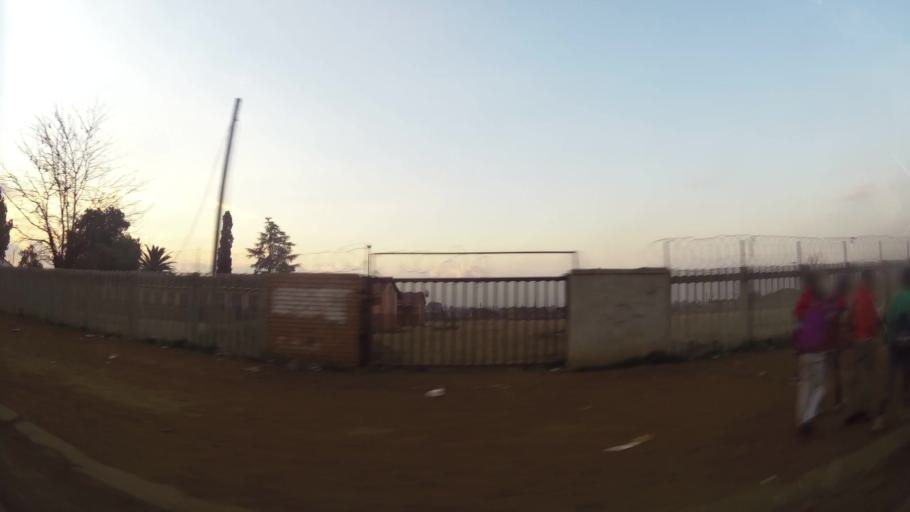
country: ZA
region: Gauteng
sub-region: City of Johannesburg Metropolitan Municipality
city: Orange Farm
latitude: -26.5543
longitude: 27.8653
